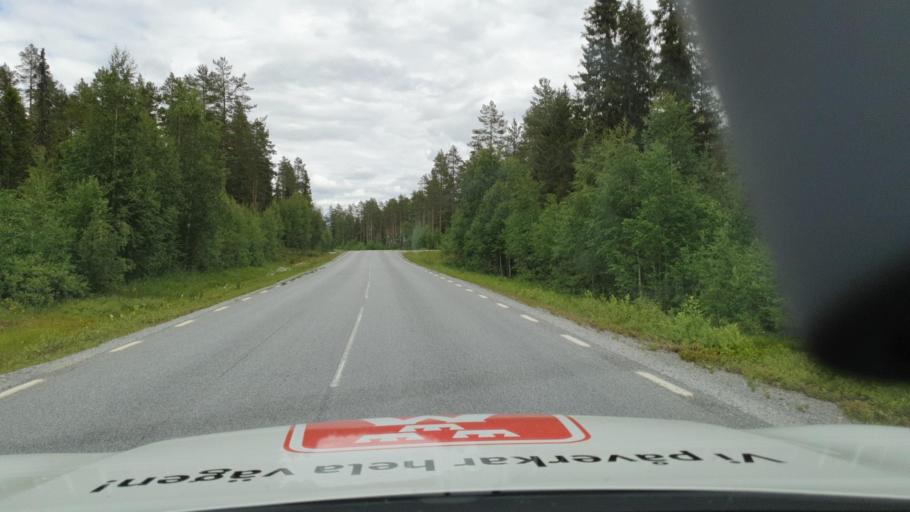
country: SE
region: Vaesterbotten
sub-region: Bjurholms Kommun
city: Bjurholm
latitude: 63.8824
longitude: 19.0571
